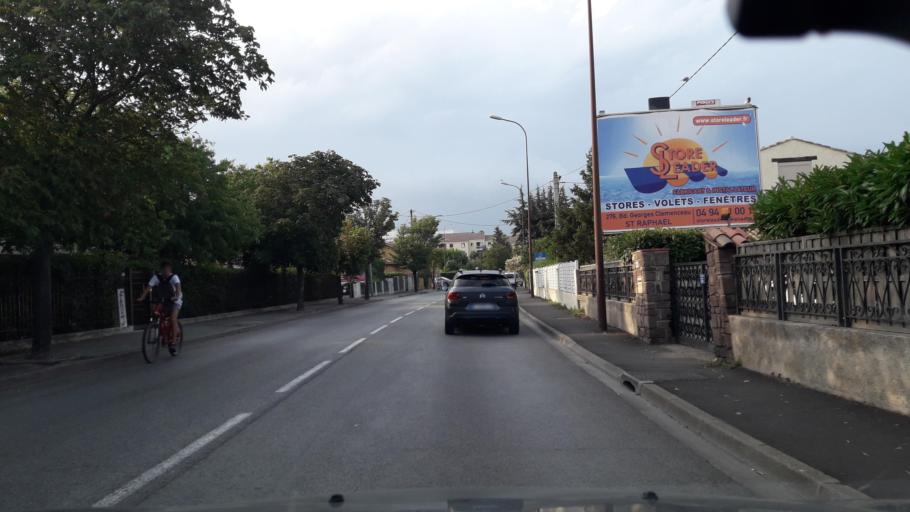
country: FR
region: Provence-Alpes-Cote d'Azur
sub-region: Departement du Var
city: Frejus
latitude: 43.4338
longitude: 6.7542
